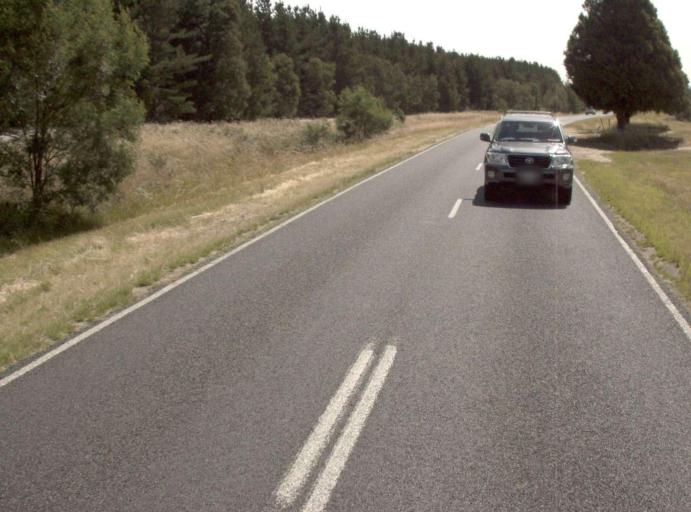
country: AU
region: Victoria
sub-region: Wellington
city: Sale
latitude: -38.1624
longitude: 146.8875
